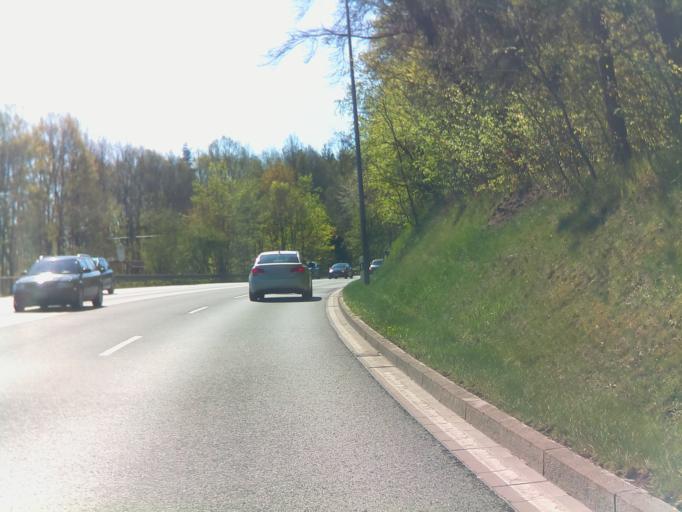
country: DE
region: Saxony
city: Plauen
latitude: 50.5198
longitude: 12.1178
